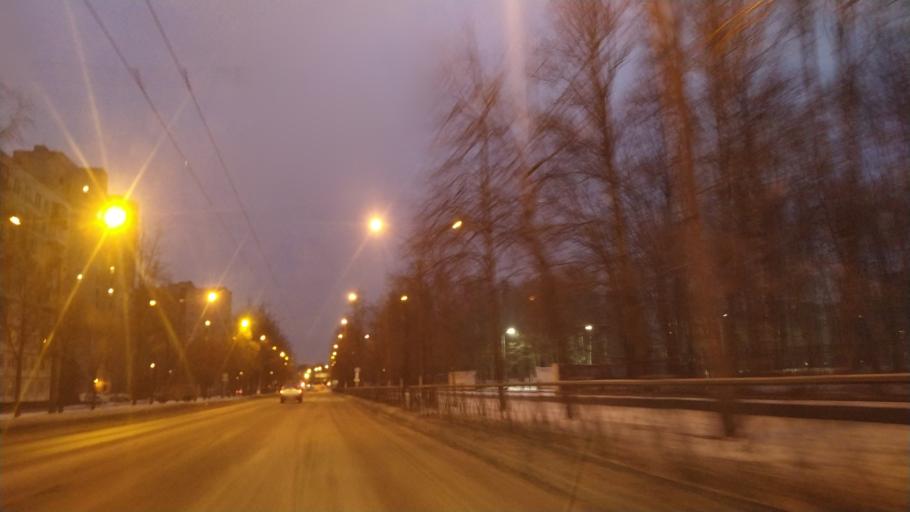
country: RU
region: Leningrad
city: Kalininskiy
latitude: 59.9661
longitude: 30.4160
